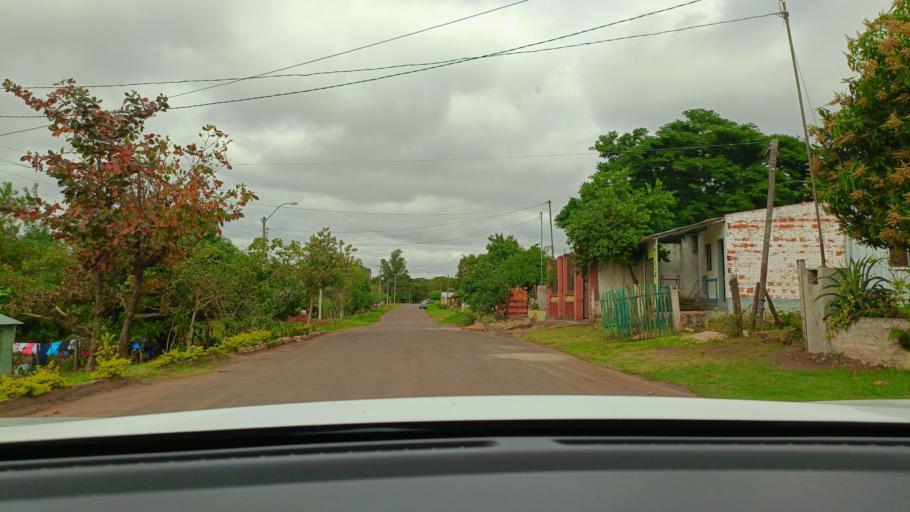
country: PY
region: San Pedro
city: Guayaybi
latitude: -24.6623
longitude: -56.4480
